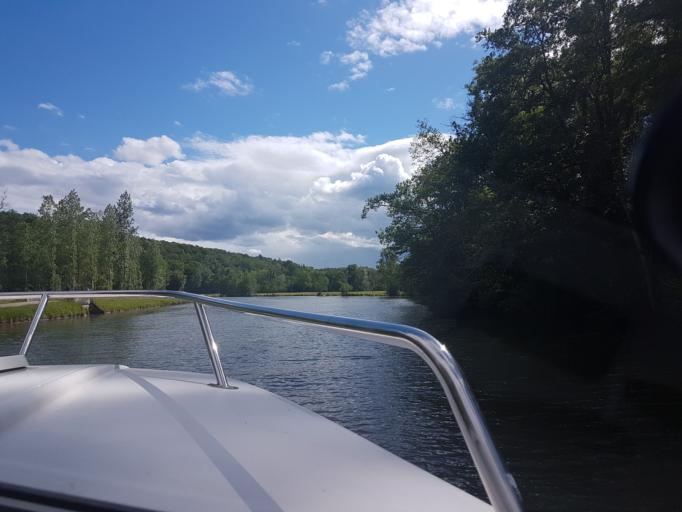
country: FR
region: Bourgogne
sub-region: Departement de l'Yonne
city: Vermenton
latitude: 47.5628
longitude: 3.6518
